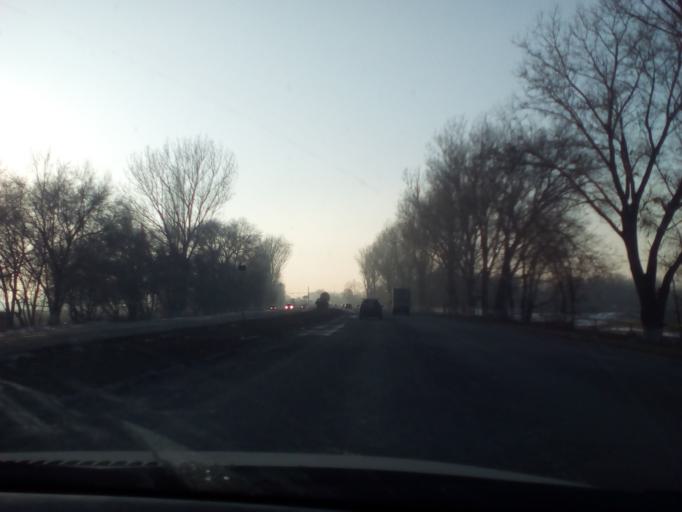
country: KZ
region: Almaty Oblysy
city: Burunday
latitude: 43.2238
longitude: 76.6057
